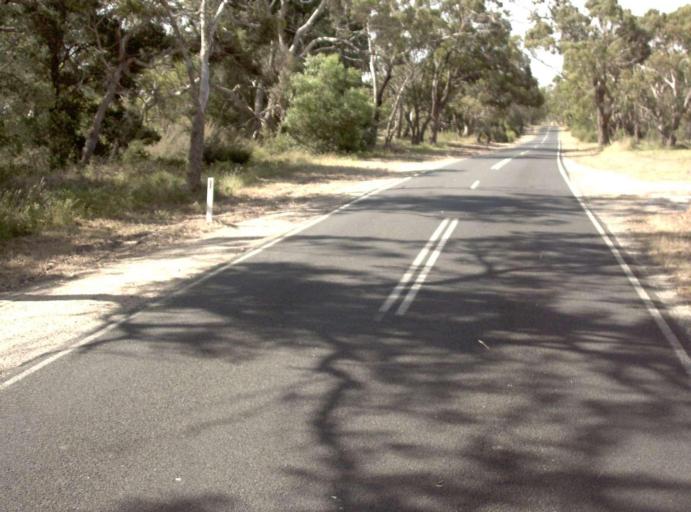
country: AU
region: Victoria
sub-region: Wellington
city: Sale
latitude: -38.2969
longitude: 147.1541
